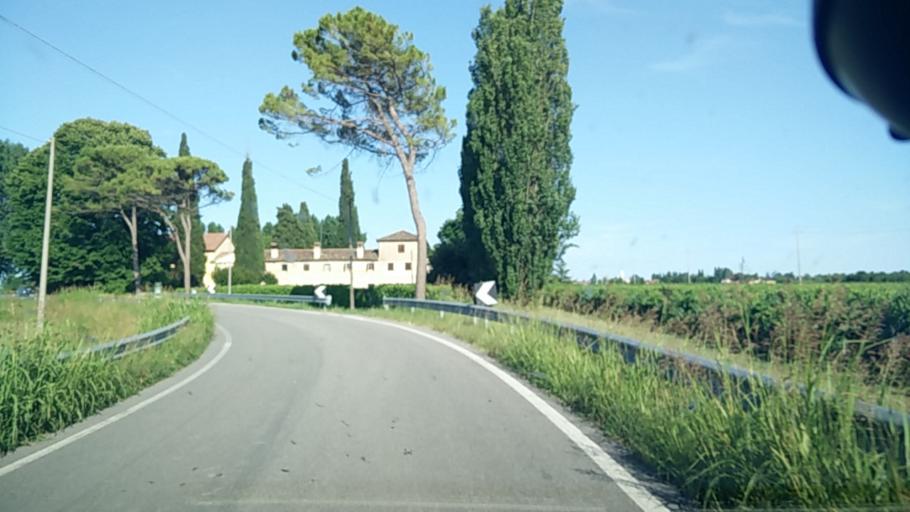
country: IT
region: Veneto
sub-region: Provincia di Treviso
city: San Biagio di Callalta
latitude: 45.6849
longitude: 12.3893
